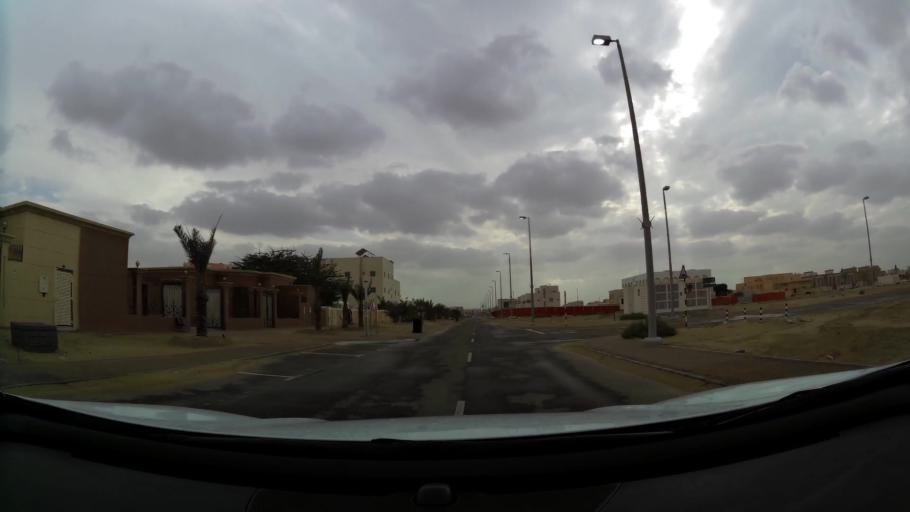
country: AE
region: Abu Dhabi
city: Abu Dhabi
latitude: 24.3514
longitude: 54.6289
